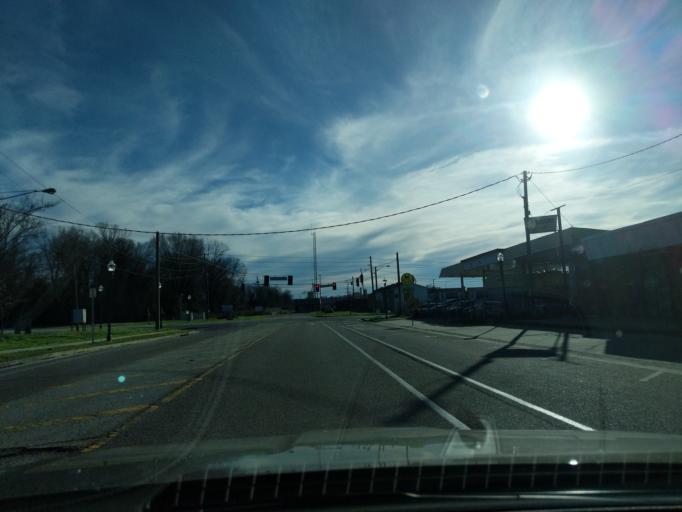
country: US
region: Georgia
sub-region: Richmond County
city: Augusta
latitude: 33.4582
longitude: -81.9534
